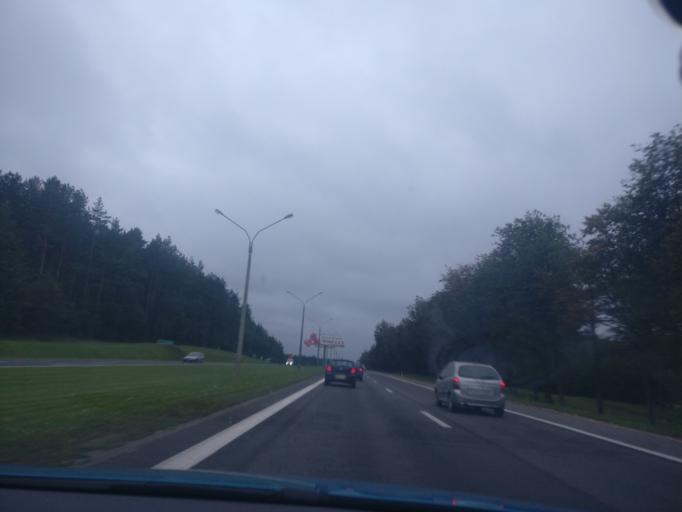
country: BY
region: Minsk
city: Korolev Stan
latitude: 53.9837
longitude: 27.7847
